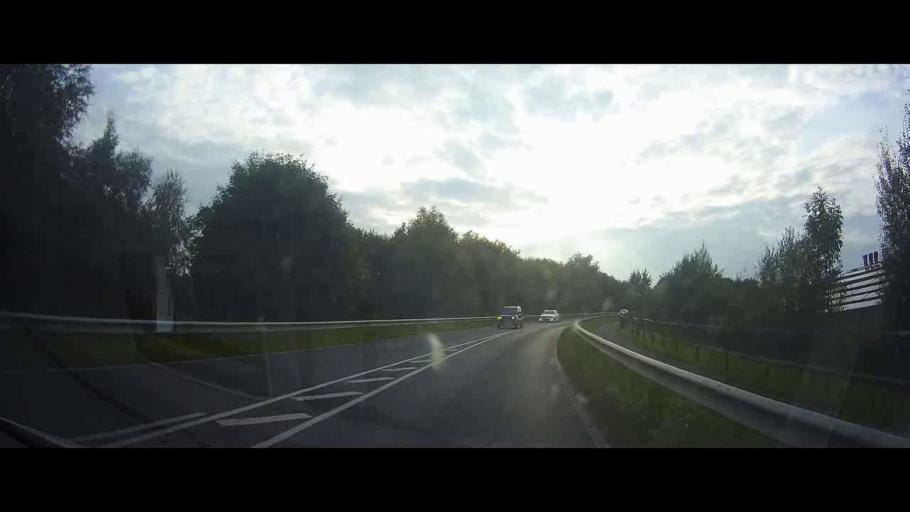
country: DE
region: Lower Saxony
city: Adelebsen
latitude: 51.5537
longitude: 9.7815
